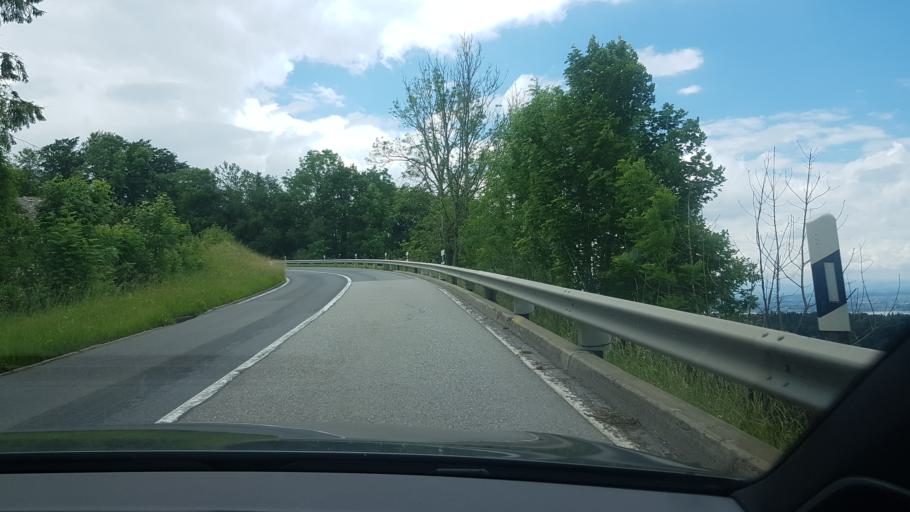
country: CH
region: Zug
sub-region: Zug
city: Menzingen
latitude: 47.1900
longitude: 8.5689
